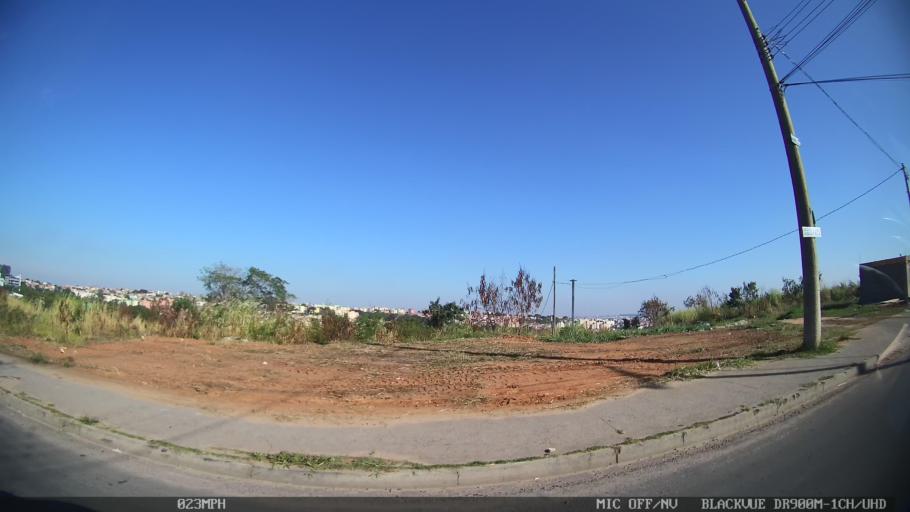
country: BR
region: Sao Paulo
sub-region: Campinas
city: Campinas
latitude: -22.9806
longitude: -47.1093
